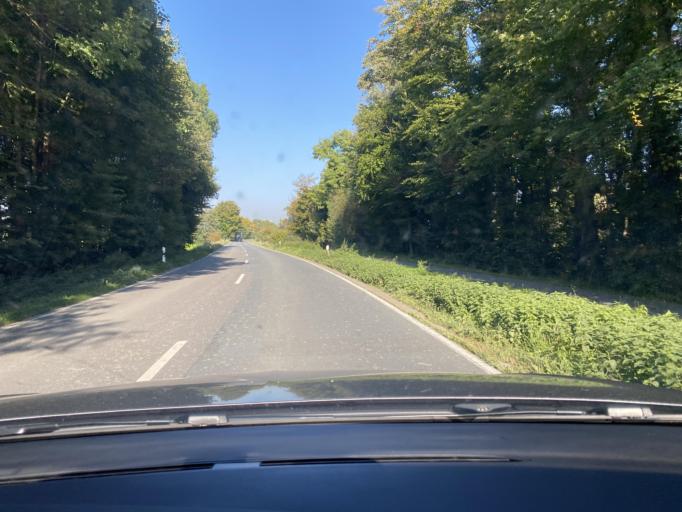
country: DE
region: North Rhine-Westphalia
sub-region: Regierungsbezirk Munster
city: Horstmar
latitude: 52.0365
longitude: 7.2752
